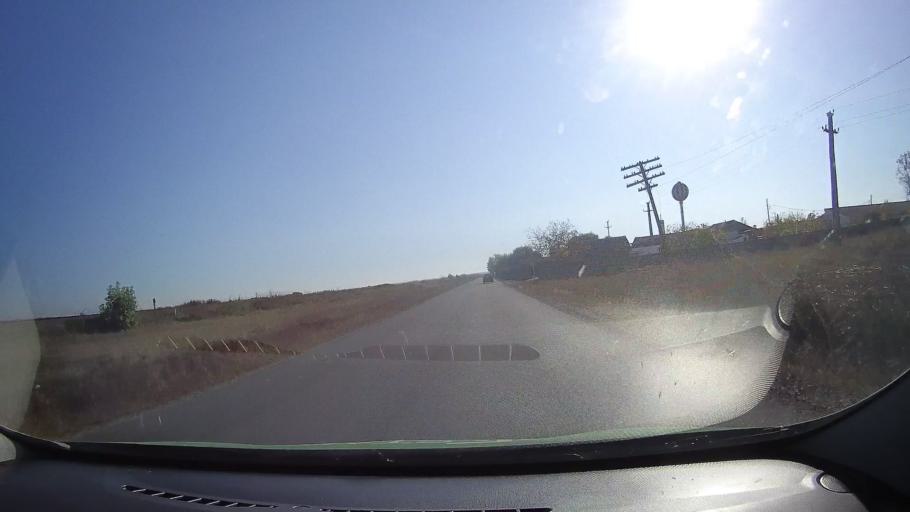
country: RO
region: Satu Mare
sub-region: Comuna Santau
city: Santau
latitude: 47.5074
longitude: 22.5253
